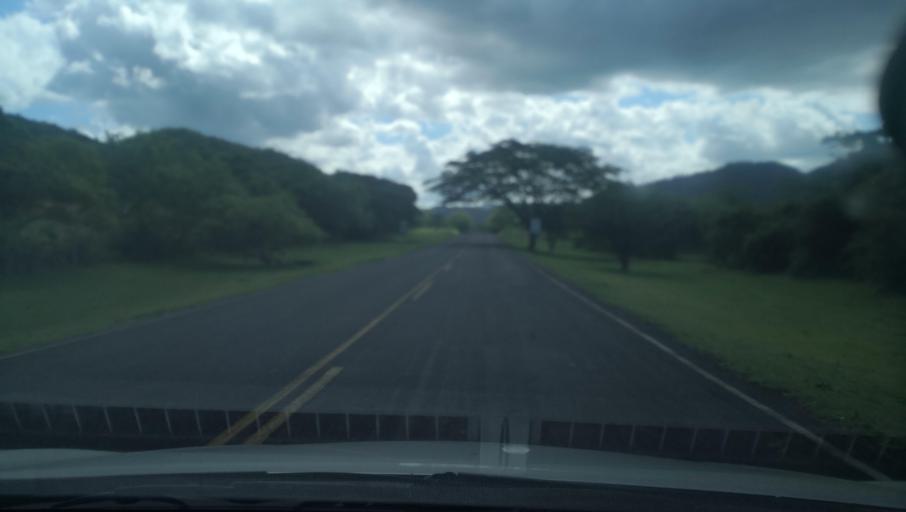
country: NI
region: Madriz
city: Somoto
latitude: 13.4656
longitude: -86.6457
